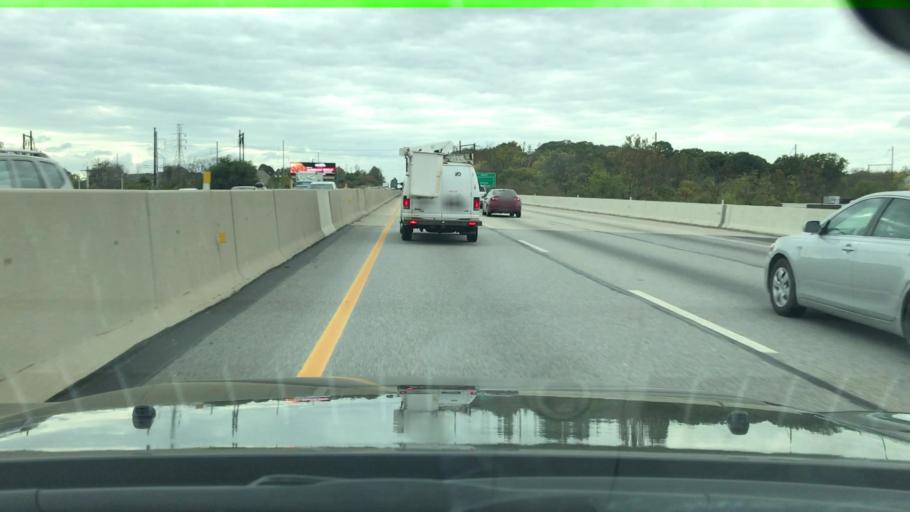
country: US
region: Pennsylvania
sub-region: Montgomery County
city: Fort Washington
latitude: 40.1313
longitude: -75.2011
